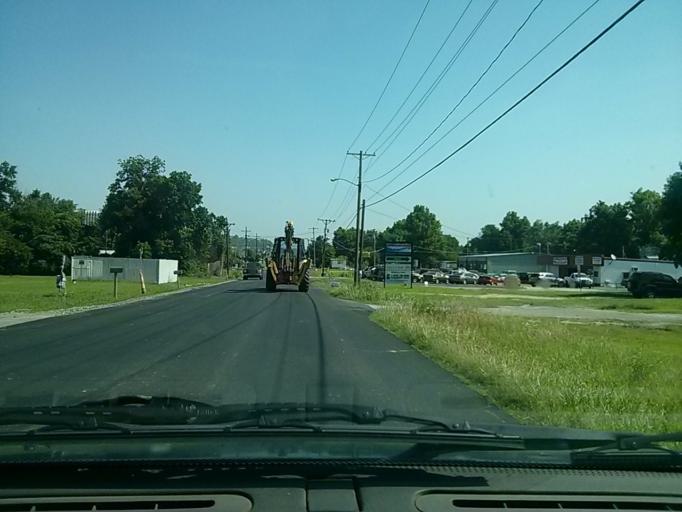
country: US
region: Oklahoma
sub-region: Rogers County
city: Catoosa
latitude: 36.1554
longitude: -95.7617
